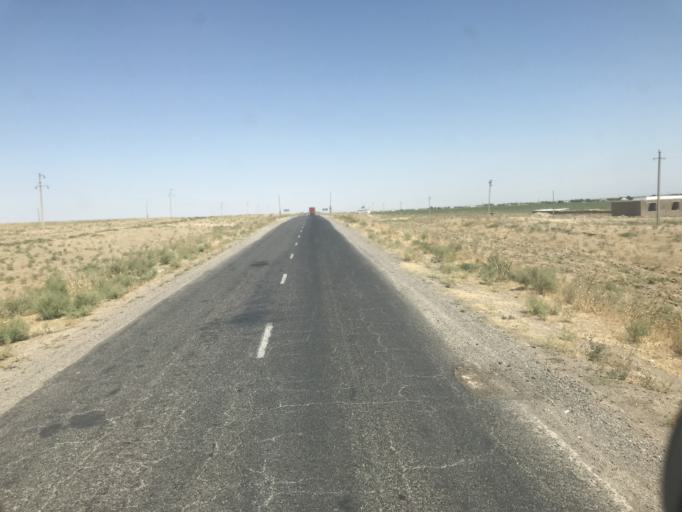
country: UZ
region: Toshkent
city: Chinoz
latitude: 41.2973
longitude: 68.6577
